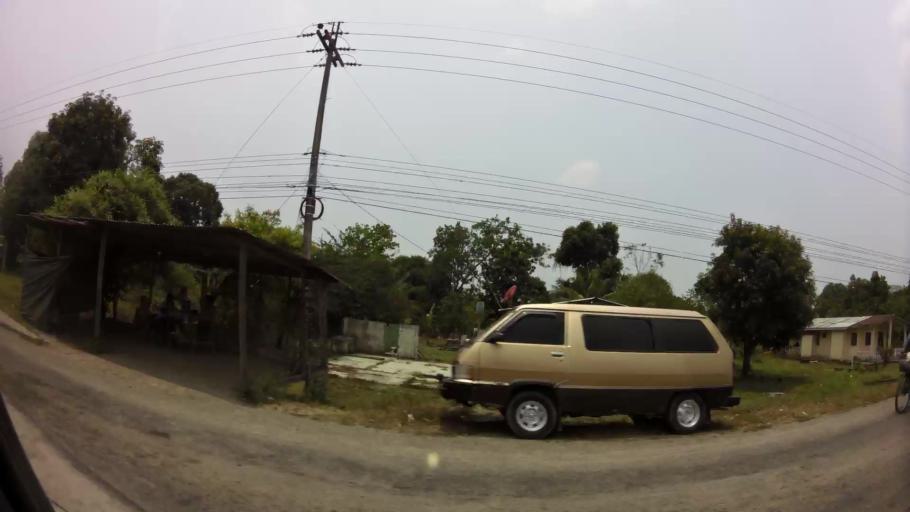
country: HN
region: Yoro
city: El Progreso
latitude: 15.4112
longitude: -87.8440
